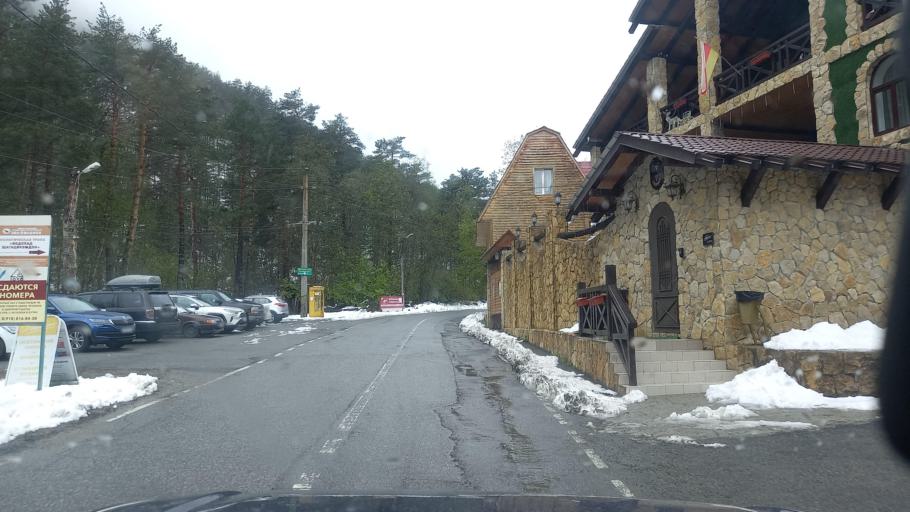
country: RU
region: North Ossetia
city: Mizur
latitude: 42.7933
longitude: 43.9230
